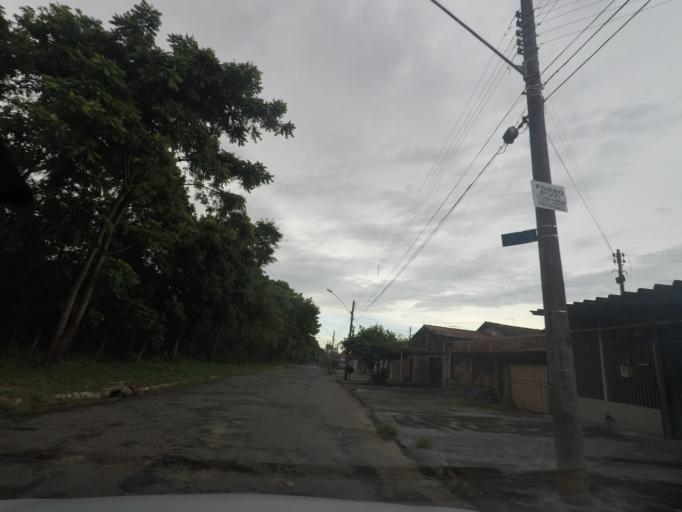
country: BR
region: Goias
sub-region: Goiania
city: Goiania
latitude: -16.7239
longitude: -49.2442
